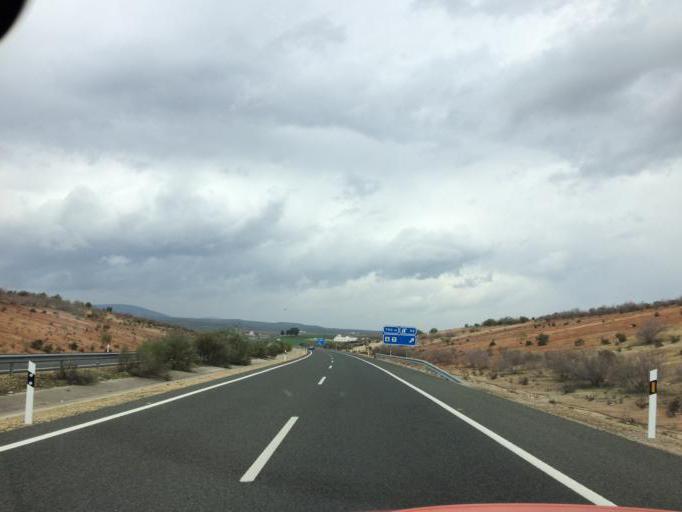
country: ES
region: Andalusia
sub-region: Provincia de Malaga
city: Antequera
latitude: 37.1014
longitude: -4.5548
